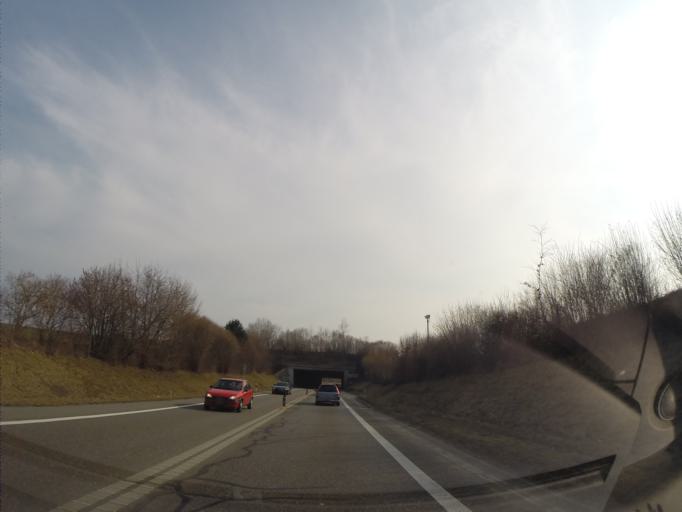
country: CH
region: Zurich
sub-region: Bezirk Winterthur
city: Hettlingen
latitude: 47.5471
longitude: 8.6887
